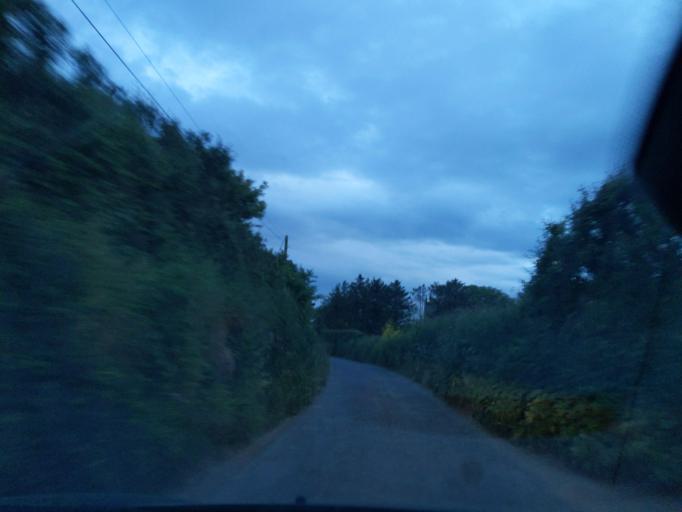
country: GB
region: England
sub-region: Cornwall
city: Wadebridge
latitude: 50.5750
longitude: -4.8296
